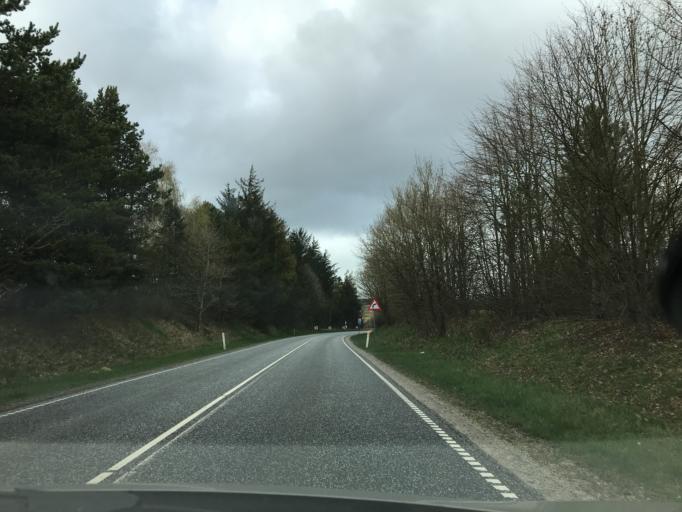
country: DK
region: Central Jutland
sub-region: Skive Kommune
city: Skive
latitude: 56.5122
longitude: 8.9529
